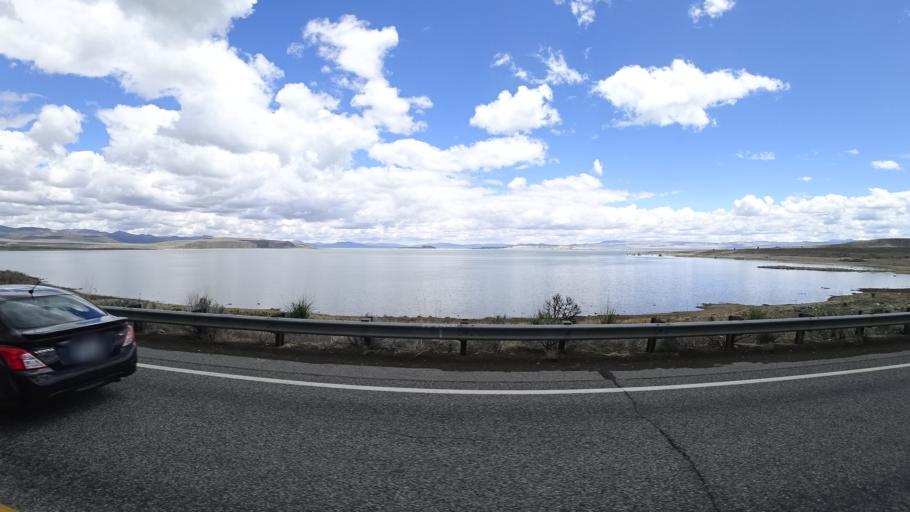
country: US
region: California
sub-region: Mono County
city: Bridgeport
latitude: 37.9818
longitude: -119.1390
